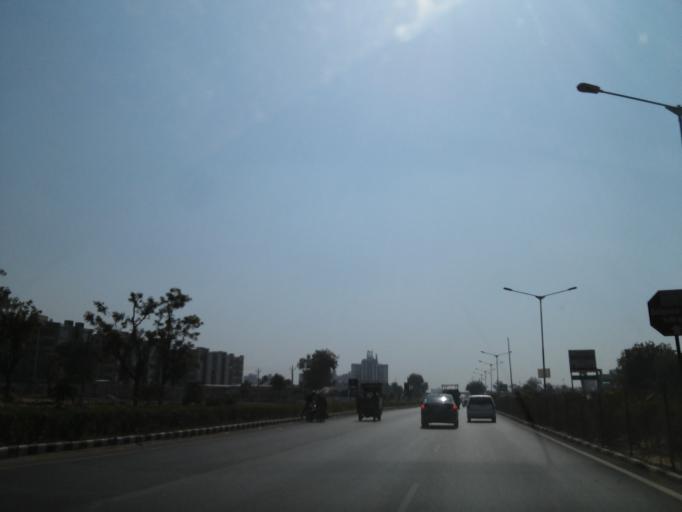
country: IN
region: Gujarat
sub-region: Gandhinagar
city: Adalaj
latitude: 23.1115
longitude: 72.5354
